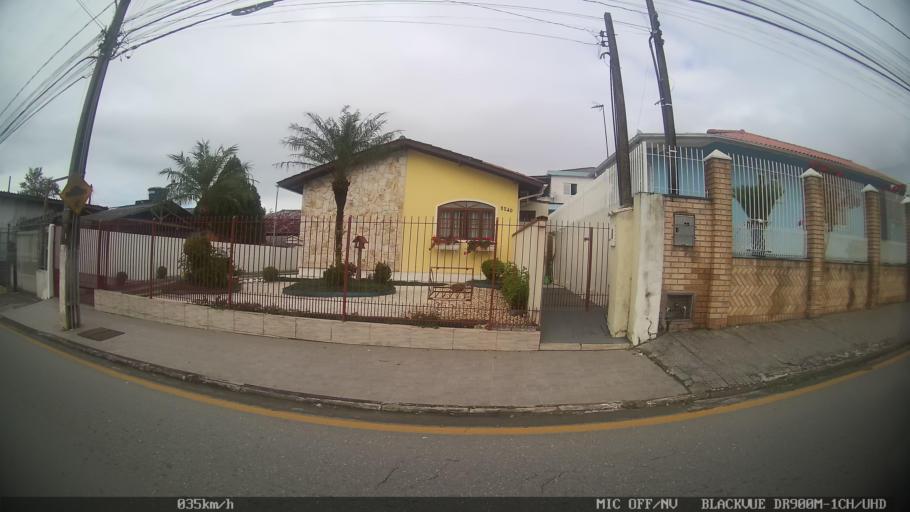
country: BR
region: Santa Catarina
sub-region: Biguacu
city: Biguacu
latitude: -27.5452
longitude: -48.6412
